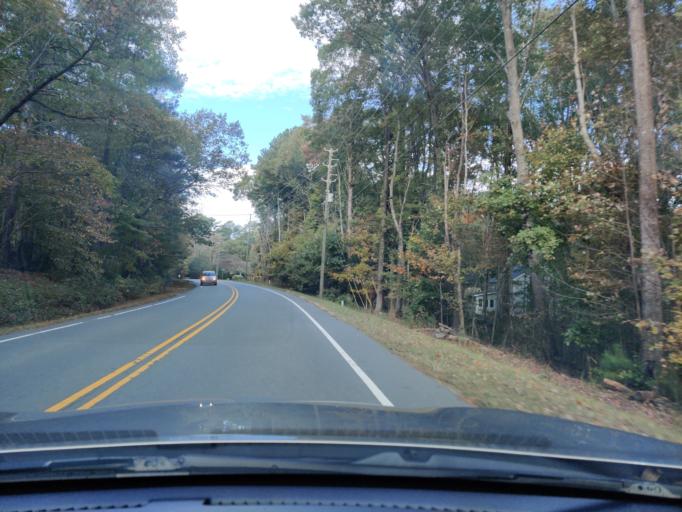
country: US
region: North Carolina
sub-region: Wake County
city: Cary
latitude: 35.9208
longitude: -78.7191
